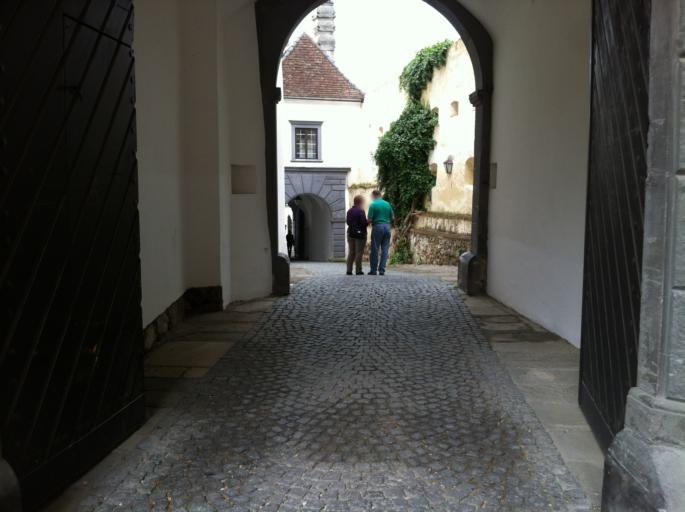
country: AT
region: Lower Austria
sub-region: Politischer Bezirk Melk
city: Melk
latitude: 48.1899
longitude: 15.3559
